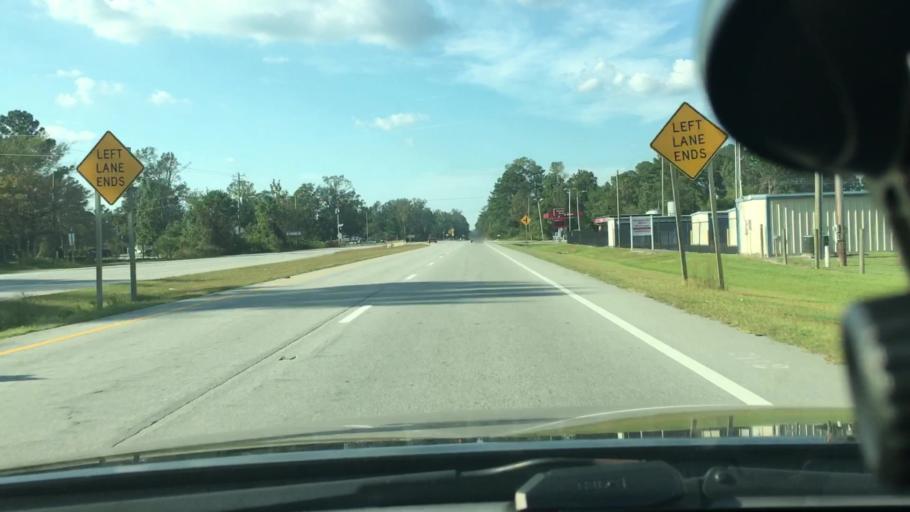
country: US
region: North Carolina
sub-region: Craven County
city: New Bern
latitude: 35.1538
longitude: -77.0352
